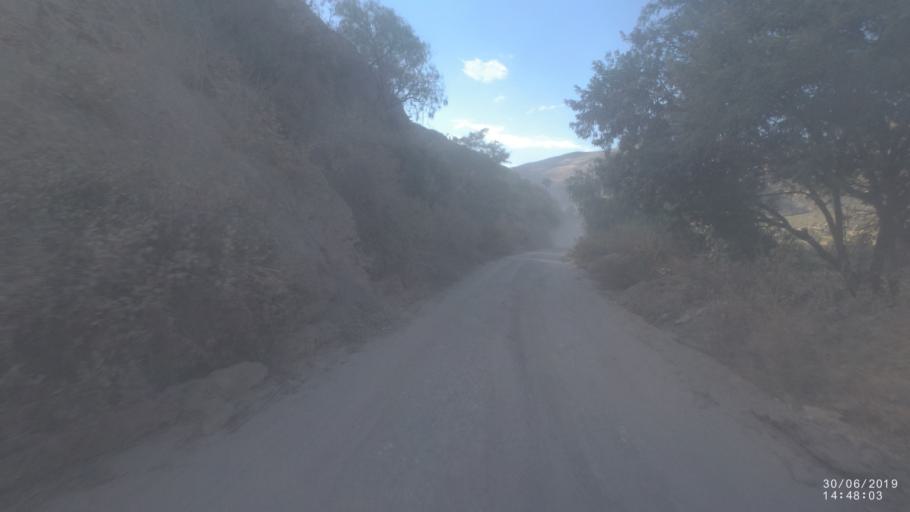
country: BO
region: Cochabamba
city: Irpa Irpa
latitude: -17.7910
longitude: -66.3447
